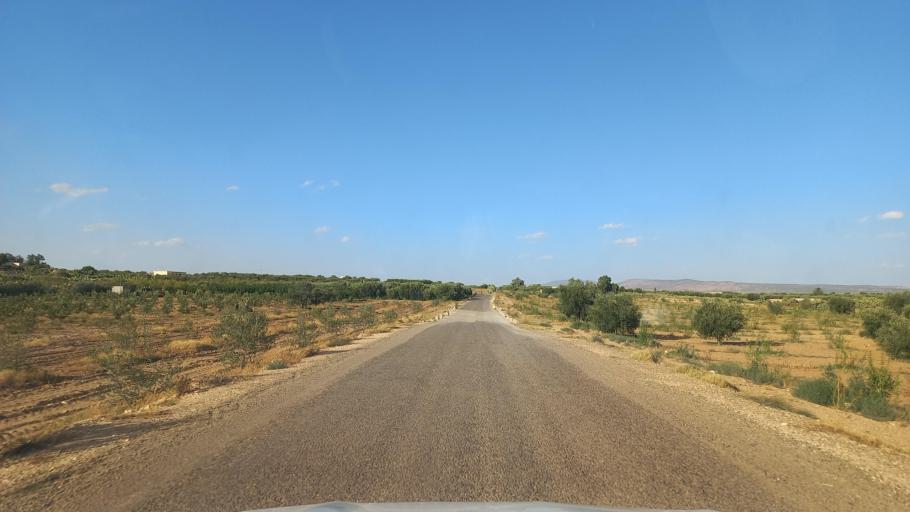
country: TN
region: Al Qasrayn
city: Kasserine
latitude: 35.2674
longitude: 9.0281
